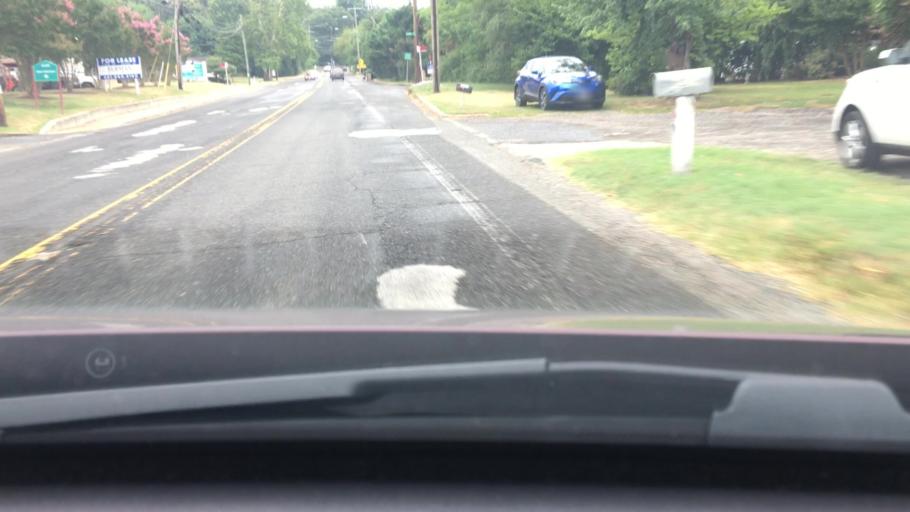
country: US
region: Maryland
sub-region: Prince George's County
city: Beltsville
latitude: 39.0458
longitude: -76.9147
